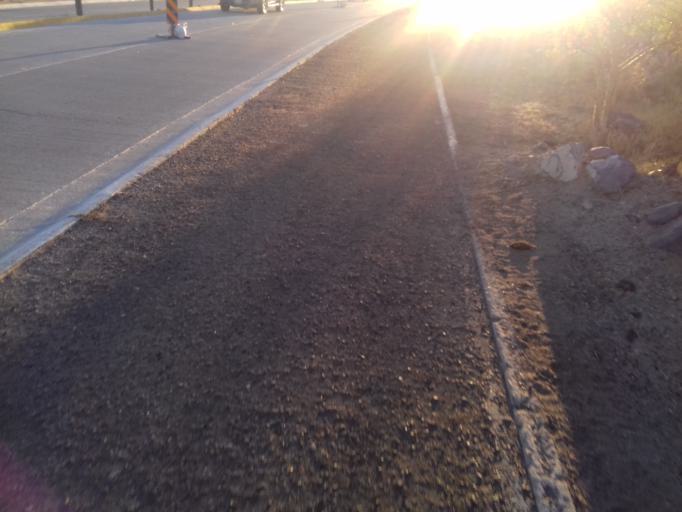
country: MX
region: Baja California Sur
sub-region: La Paz
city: La Paz
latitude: 24.0884
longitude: -110.3061
